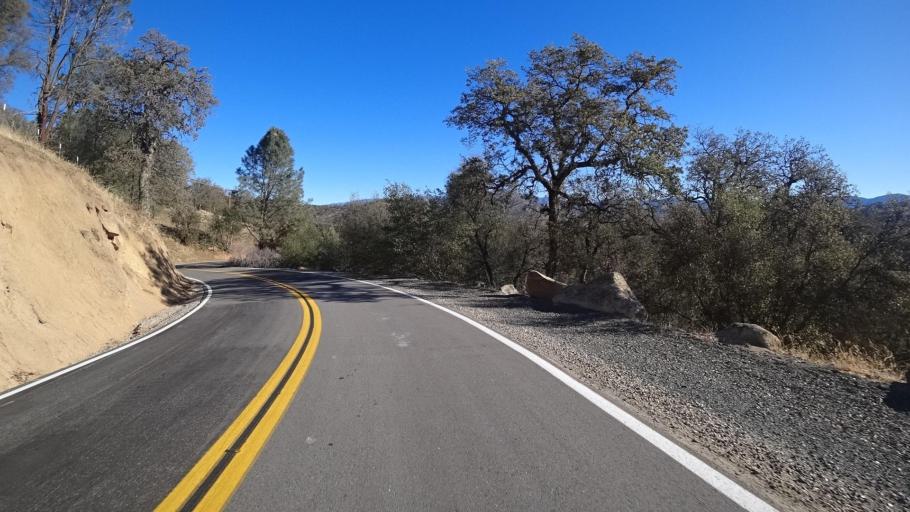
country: US
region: California
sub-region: Kern County
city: Alta Sierra
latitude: 35.7070
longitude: -118.7447
